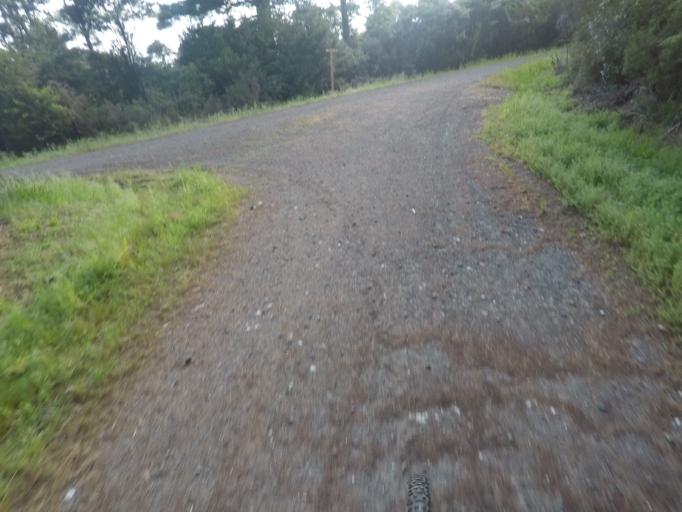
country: NZ
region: Auckland
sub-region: Auckland
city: Parakai
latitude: -36.7081
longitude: 174.5801
